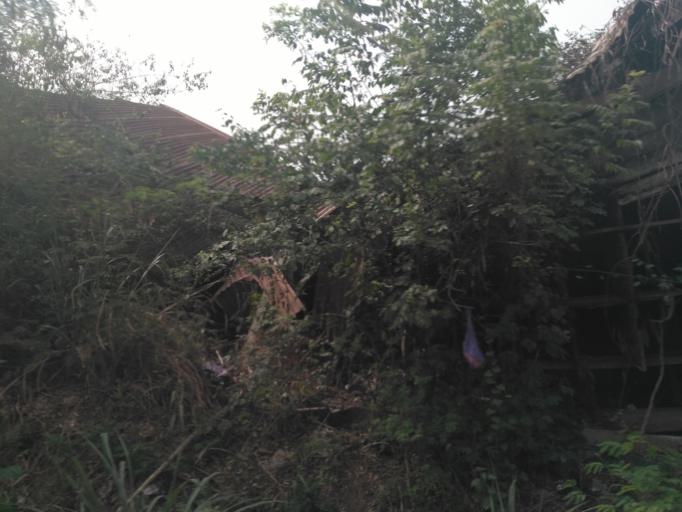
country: GH
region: Ashanti
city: Kumasi
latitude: 6.6766
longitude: -1.5992
